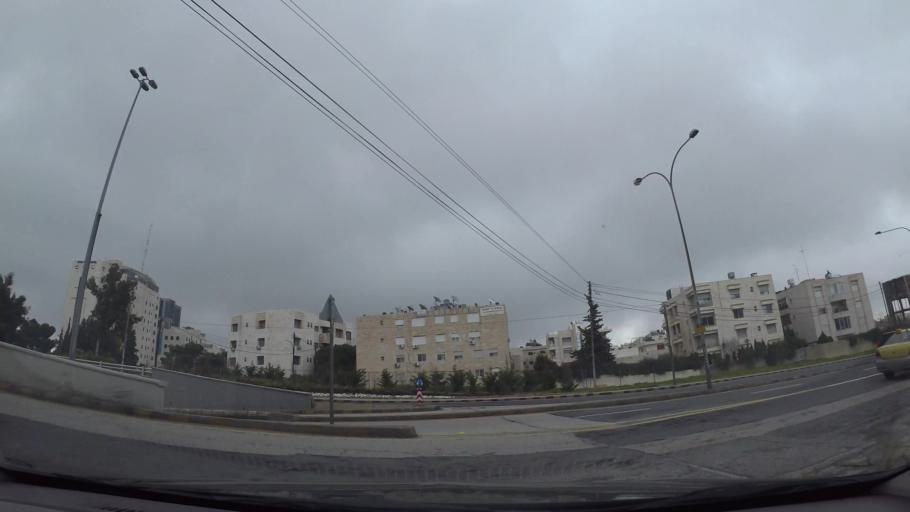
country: JO
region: Amman
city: Wadi as Sir
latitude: 31.9593
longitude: 35.8705
